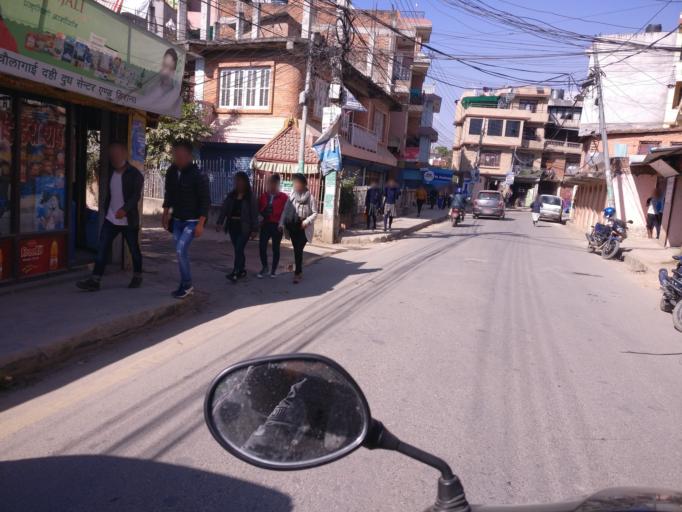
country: NP
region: Central Region
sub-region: Bagmati Zone
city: Patan
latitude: 27.6600
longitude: 85.3173
